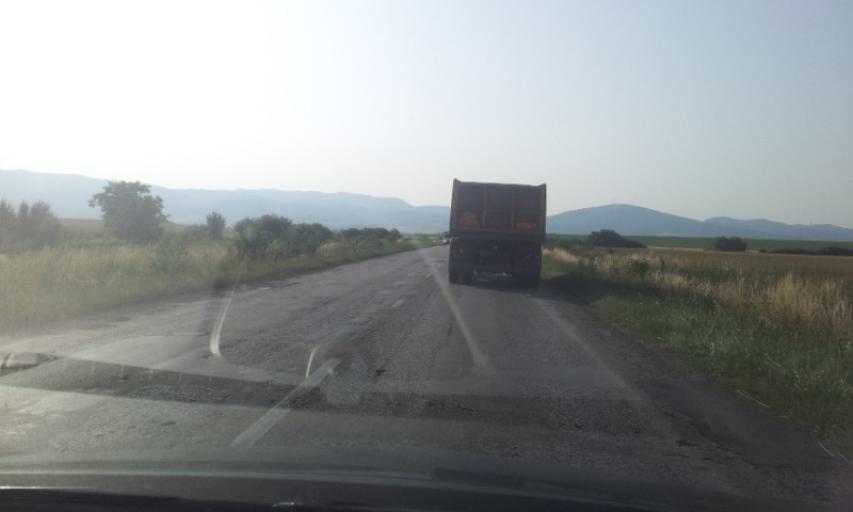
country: SK
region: Kosicky
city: Kosice
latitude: 48.6106
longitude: 21.2862
